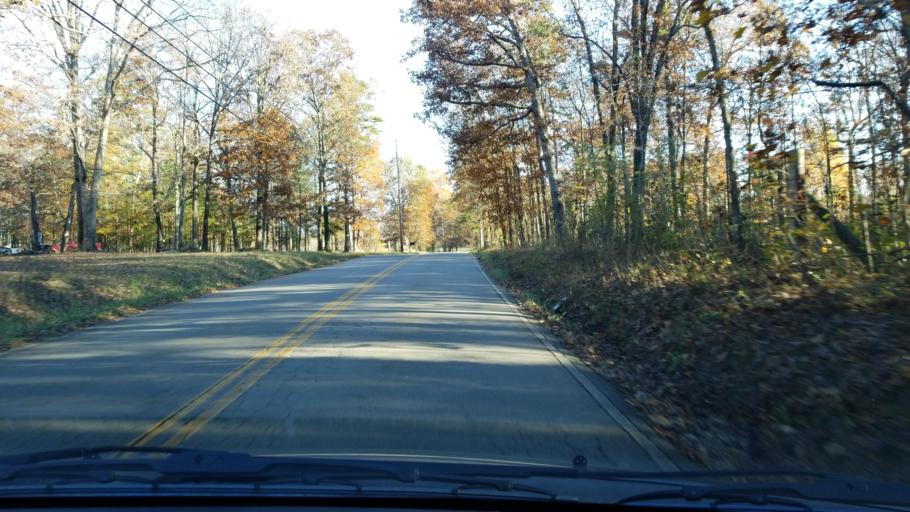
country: US
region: Tennessee
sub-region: Hamilton County
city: Falling Water
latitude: 35.2225
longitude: -85.2789
